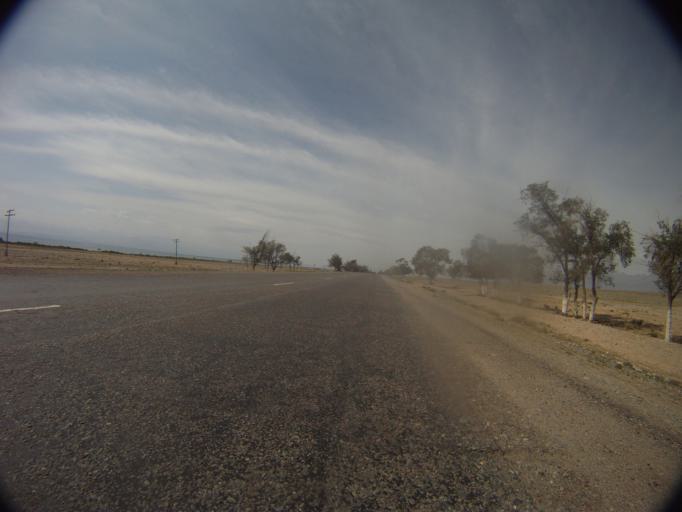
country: KG
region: Ysyk-Koel
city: Balykchy
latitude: 42.5134
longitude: 76.5233
